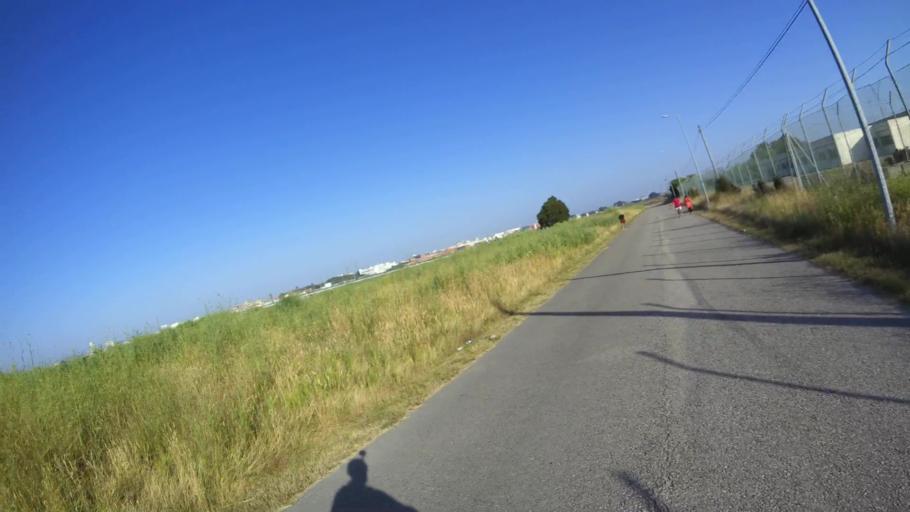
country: PT
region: Aveiro
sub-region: Aveiro
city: Aveiro
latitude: 40.6387
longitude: -8.6710
